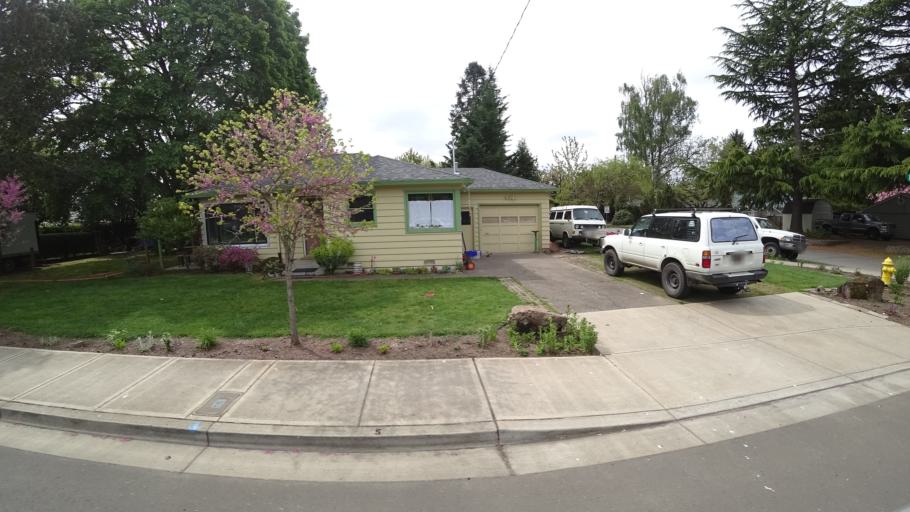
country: US
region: Oregon
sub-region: Washington County
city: Hillsboro
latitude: 45.5279
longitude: -122.9960
